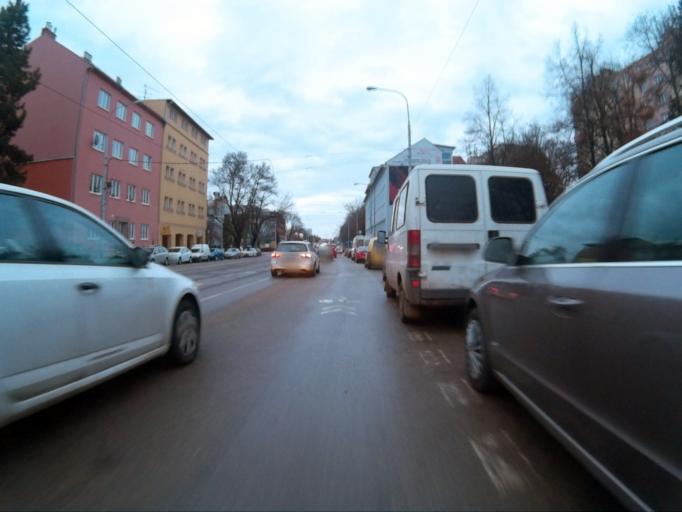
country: CZ
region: South Moravian
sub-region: Mesto Brno
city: Brno
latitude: 49.1817
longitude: 16.5948
